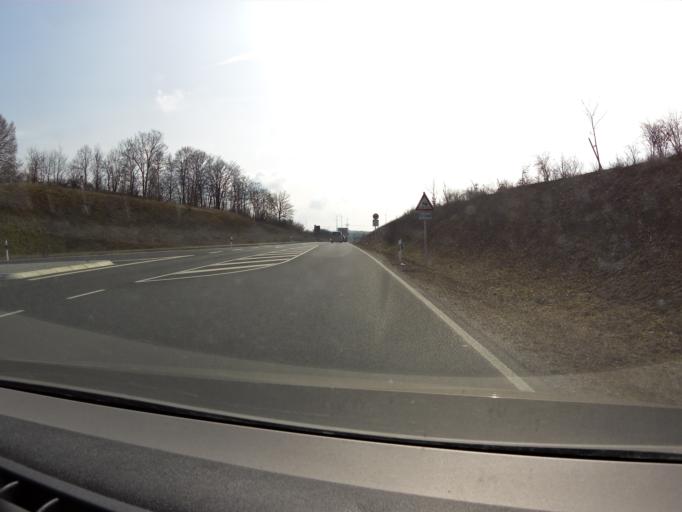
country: DE
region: Bavaria
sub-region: Regierungsbezirk Unterfranken
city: Werneck
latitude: 49.9731
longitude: 10.0917
